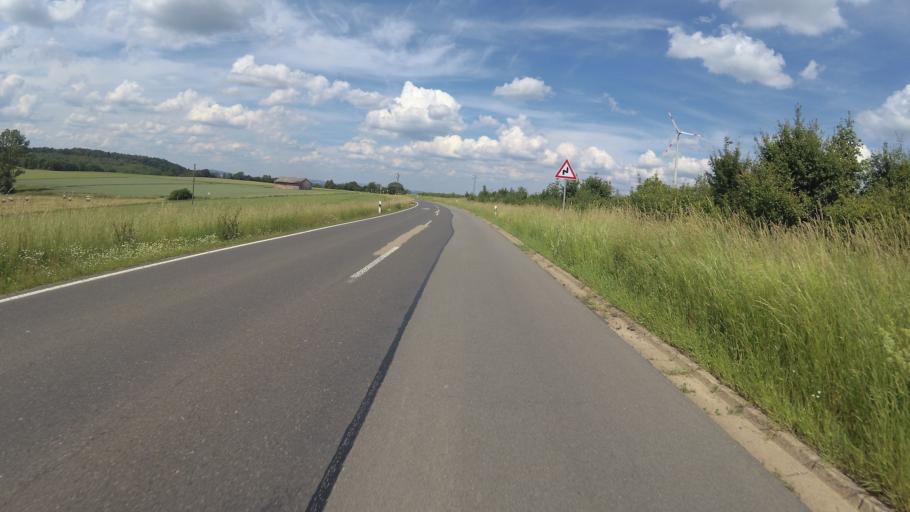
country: DE
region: Rheinland-Pfalz
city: Langwieden
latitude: 49.3758
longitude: 7.5108
